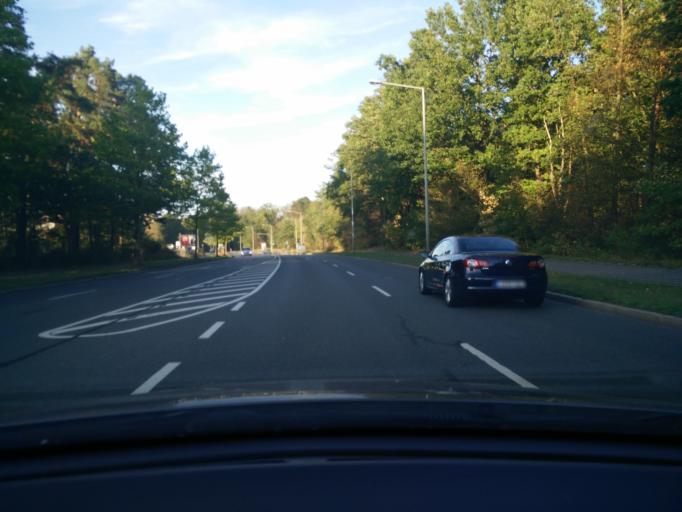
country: DE
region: Bavaria
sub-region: Regierungsbezirk Mittelfranken
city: Wendelstein
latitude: 49.3990
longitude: 11.1252
